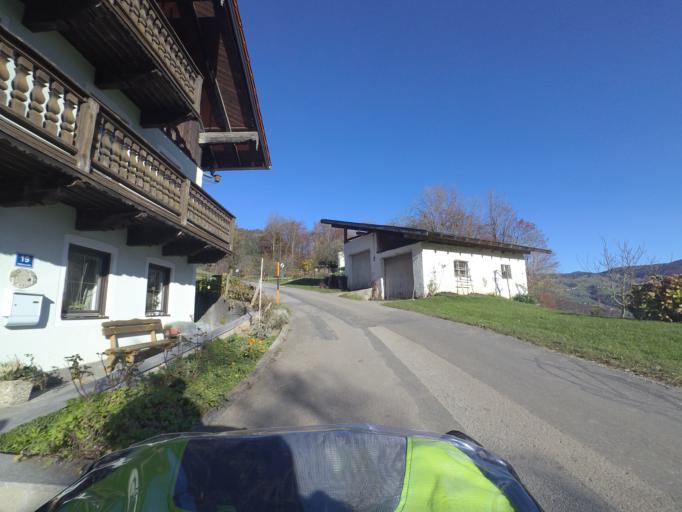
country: AT
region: Salzburg
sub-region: Politischer Bezirk Hallein
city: Puch bei Hallein
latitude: 47.7290
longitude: 13.1188
